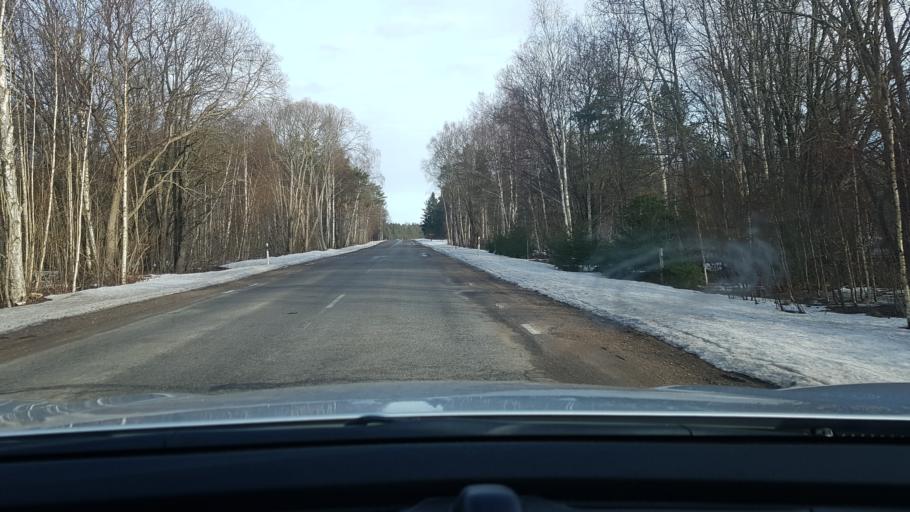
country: EE
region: Saare
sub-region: Kuressaare linn
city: Kuressaare
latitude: 58.3745
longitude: 22.6228
